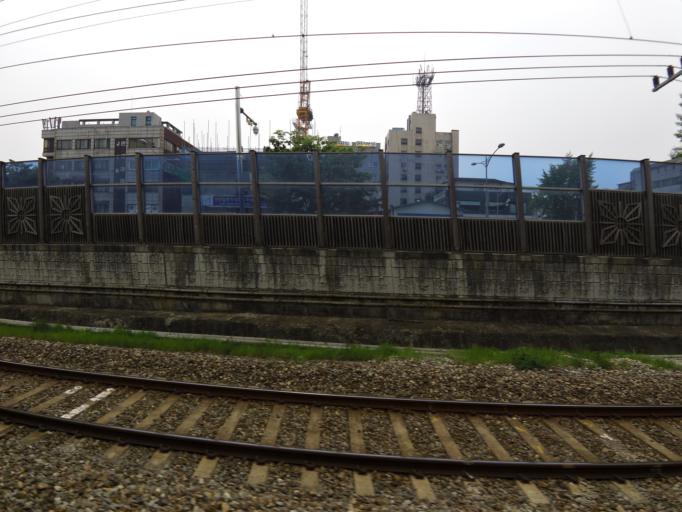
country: KR
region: Gyeonggi-do
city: Anyang-si
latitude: 37.3984
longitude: 126.9254
